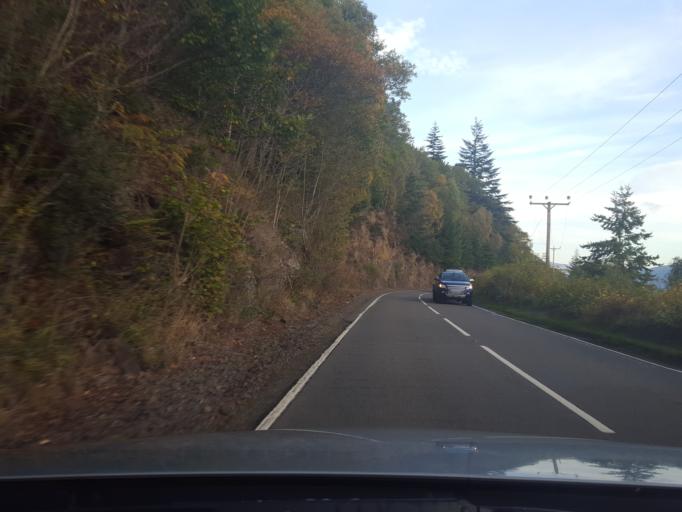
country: GB
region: Scotland
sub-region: Highland
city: Beauly
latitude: 57.2392
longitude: -4.5543
